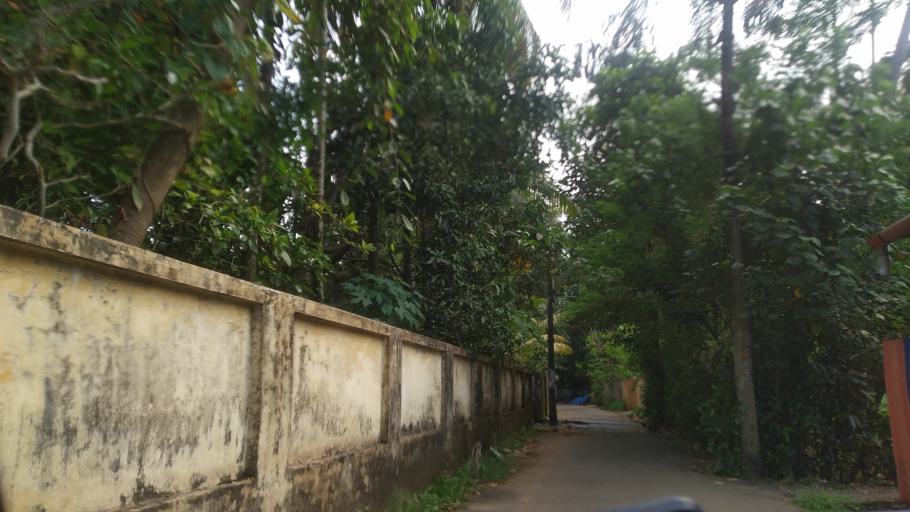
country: IN
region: Kerala
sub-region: Ernakulam
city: Elur
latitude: 10.0868
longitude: 76.2104
